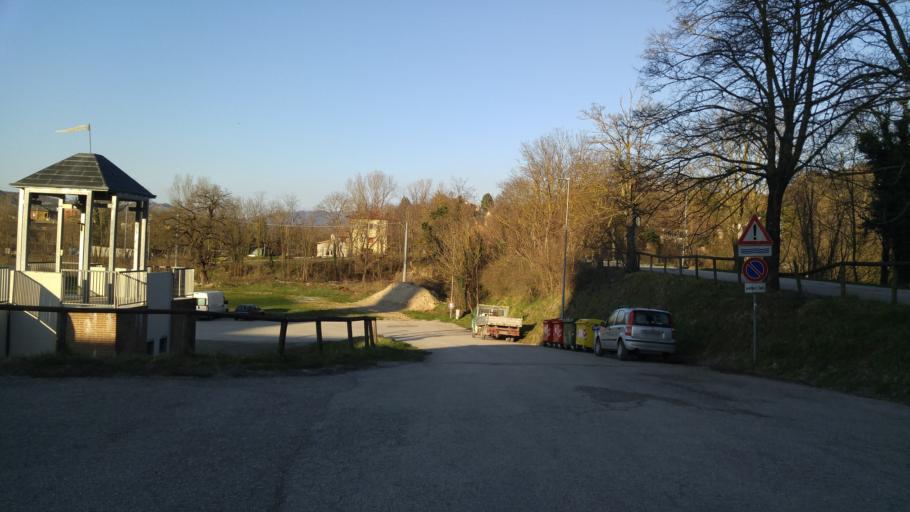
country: IT
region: The Marches
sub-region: Provincia di Pesaro e Urbino
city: Cagli
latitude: 43.5484
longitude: 12.6521
